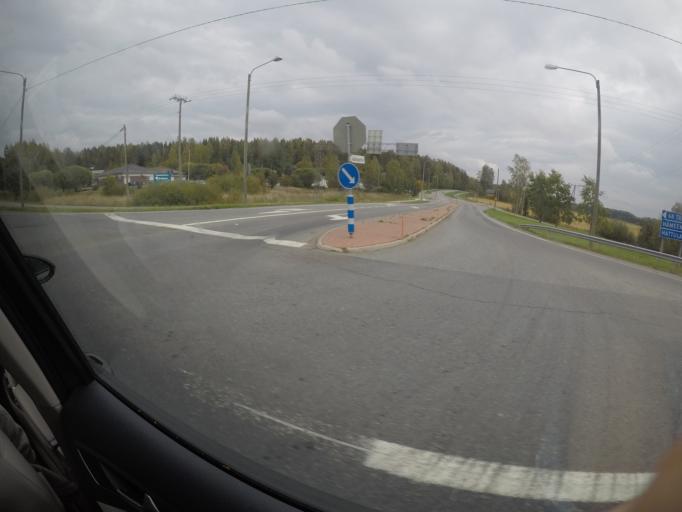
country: FI
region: Haeme
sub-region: Haemeenlinna
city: Parola
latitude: 61.0731
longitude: 24.3916
